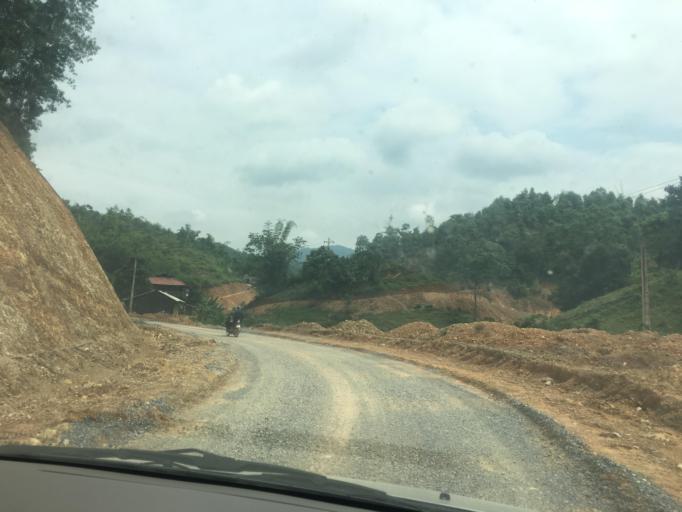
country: VN
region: Bac Kan
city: Yen Lac
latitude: 22.1581
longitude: 106.3066
